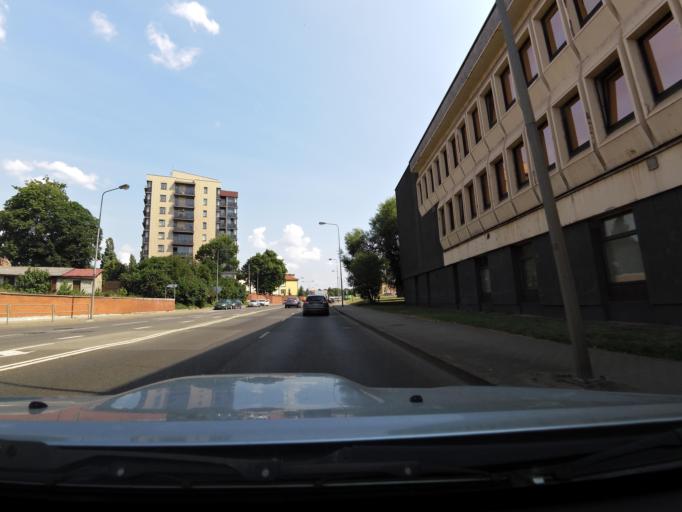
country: LT
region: Klaipedos apskritis
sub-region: Klaipeda
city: Klaipeda
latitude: 55.7197
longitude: 21.1204
